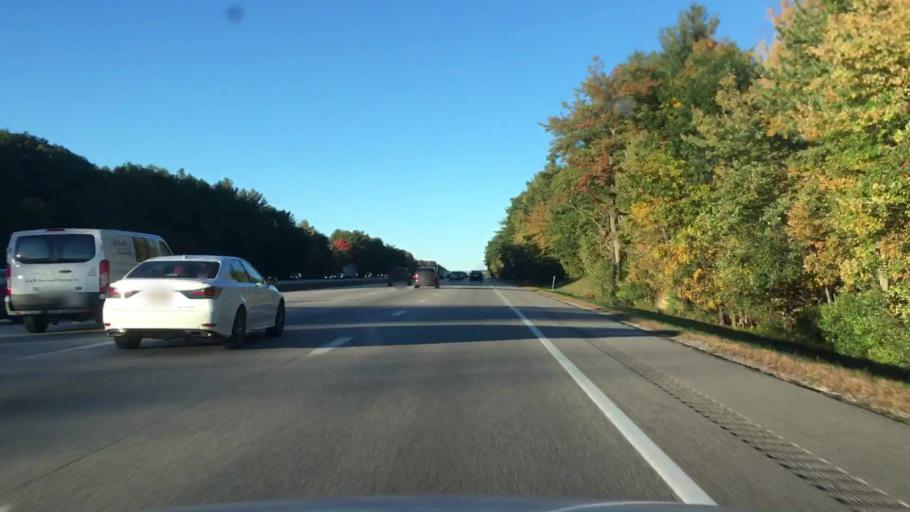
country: US
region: New Hampshire
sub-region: Rockingham County
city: Greenland
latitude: 43.0094
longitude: -70.8377
